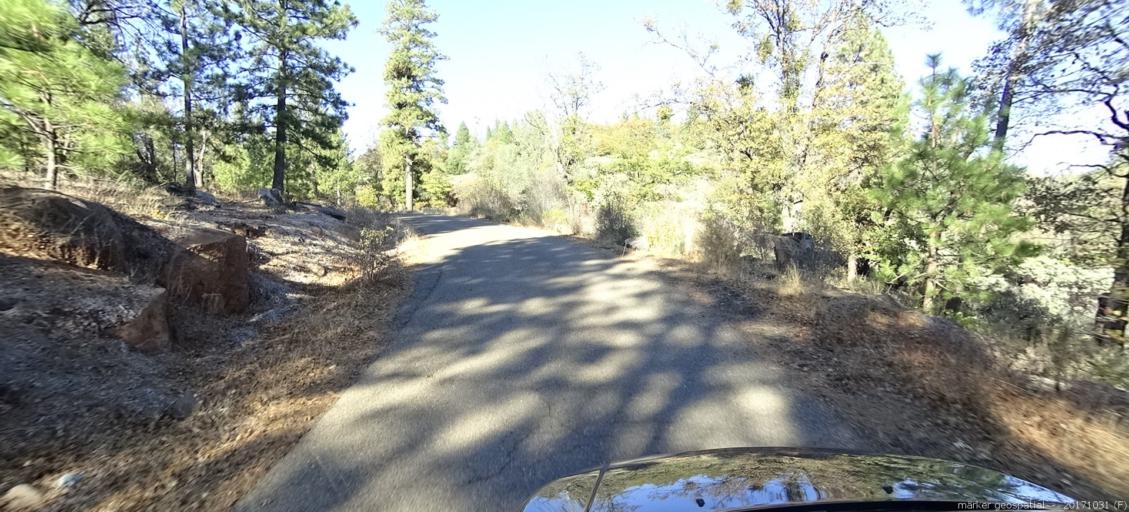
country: US
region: California
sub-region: Shasta County
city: Shingletown
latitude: 40.4809
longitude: -121.9293
